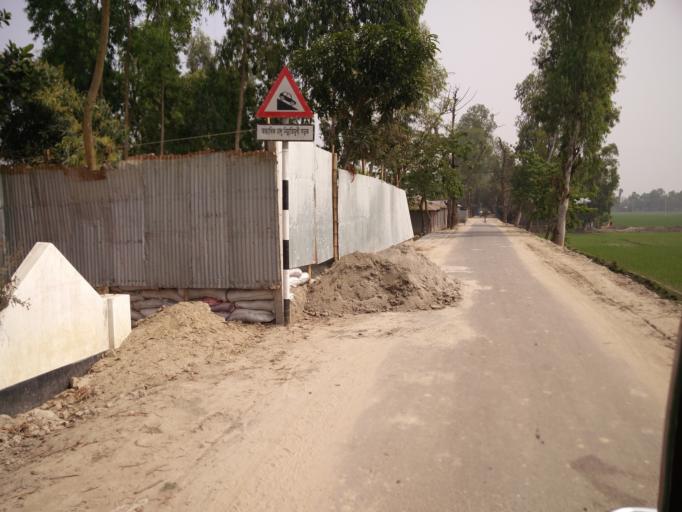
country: BD
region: Rangpur Division
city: Nageswari
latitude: 25.8864
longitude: 89.7379
